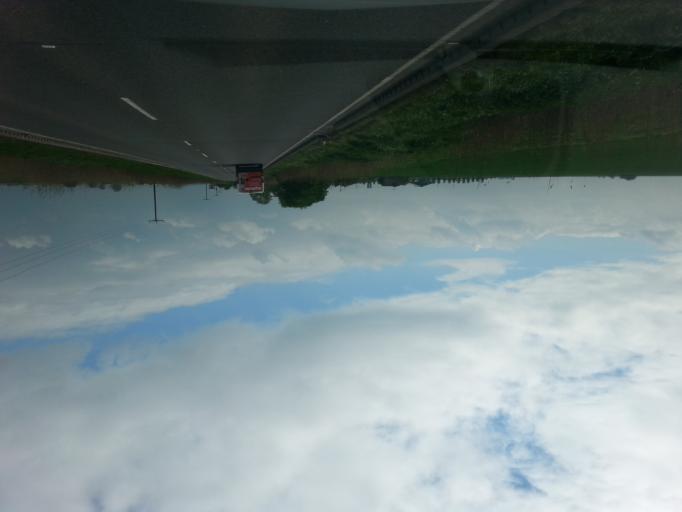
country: GB
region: England
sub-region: Cambridgeshire
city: March
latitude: 52.6089
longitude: 0.0454
